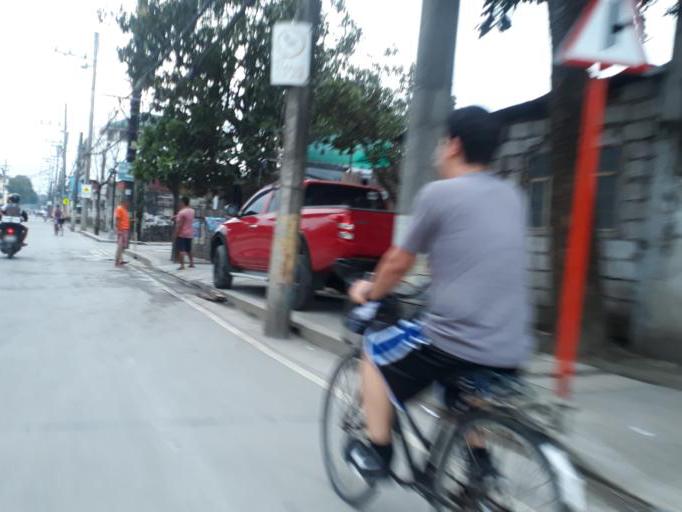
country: PH
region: Calabarzon
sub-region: Province of Rizal
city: Valenzuela
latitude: 14.7005
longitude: 120.9509
